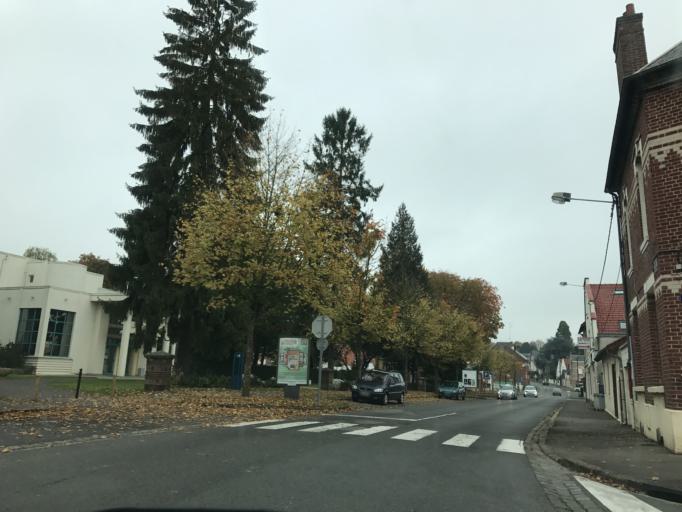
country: FR
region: Picardie
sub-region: Departement de la Somme
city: Peronne
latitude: 49.9297
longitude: 2.9323
